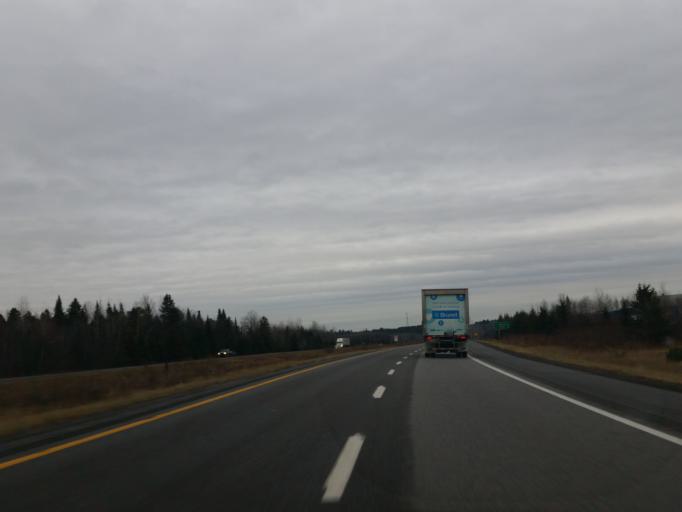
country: CA
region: Quebec
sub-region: Capitale-Nationale
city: Cap-Sante
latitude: 46.6965
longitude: -71.9040
